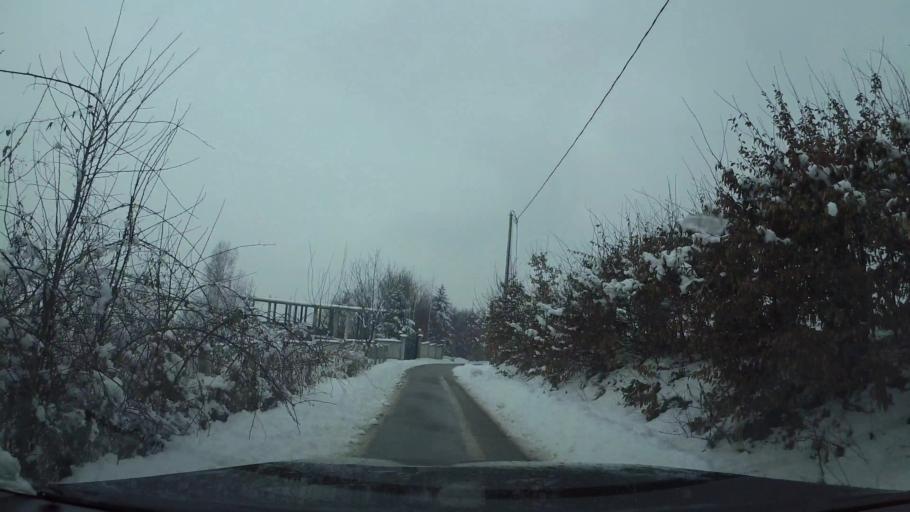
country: BA
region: Federation of Bosnia and Herzegovina
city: Hadzici
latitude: 43.8542
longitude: 18.2646
